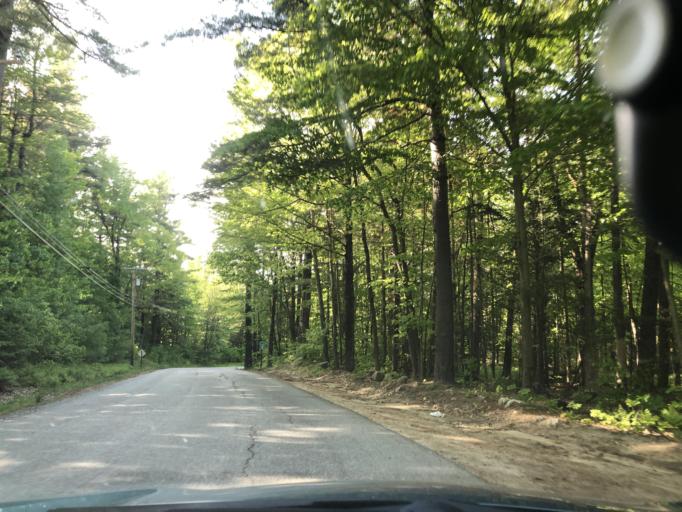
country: US
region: New Hampshire
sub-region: Merrimack County
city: New London
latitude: 43.4205
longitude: -71.9798
